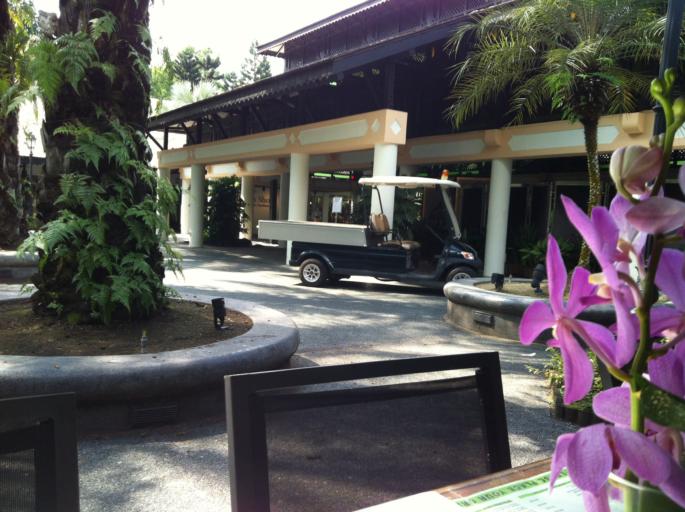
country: SG
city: Singapore
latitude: 1.3151
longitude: 103.8163
